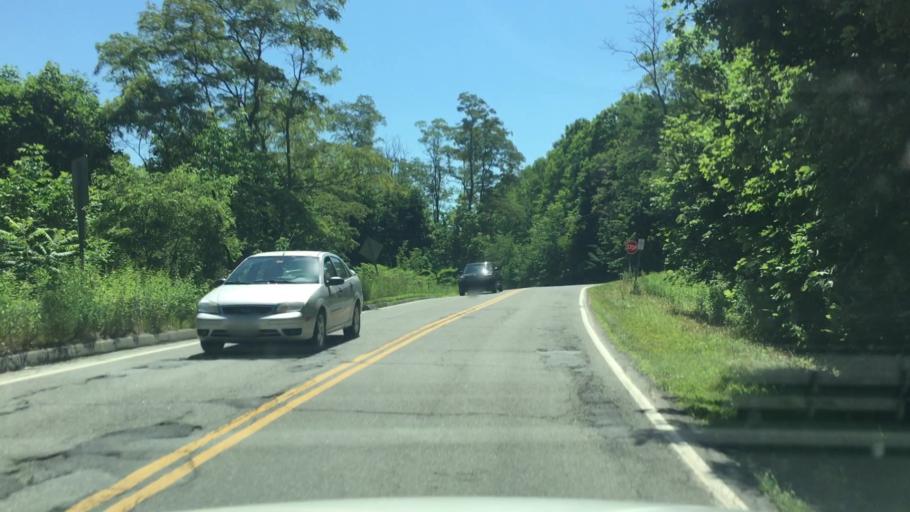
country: US
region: Maine
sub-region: Penobscot County
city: Bangor
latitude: 44.8125
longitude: -68.7824
